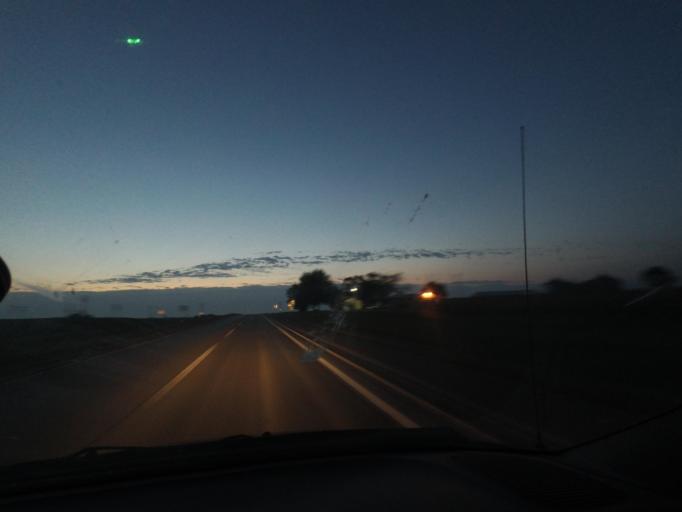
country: US
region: Missouri
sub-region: Linn County
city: Linneus
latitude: 39.7773
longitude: -93.3459
